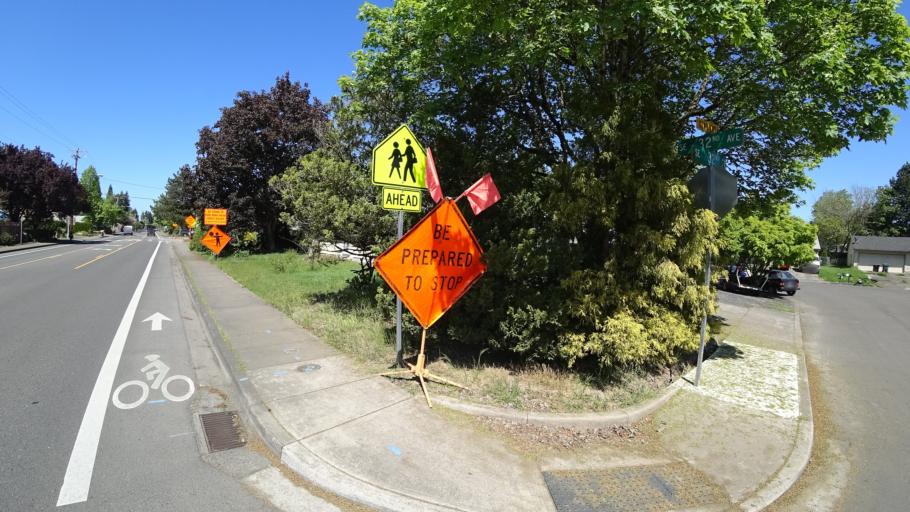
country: US
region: Oregon
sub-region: Washington County
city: Hillsboro
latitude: 45.5154
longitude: -122.9496
